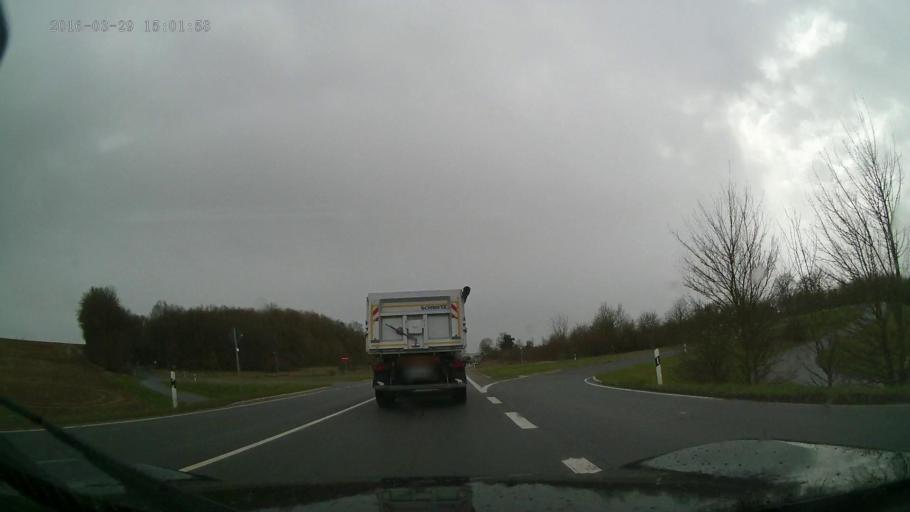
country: DE
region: Baden-Wuerttemberg
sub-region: Karlsruhe Region
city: Walldurn
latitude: 49.5649
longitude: 9.3624
